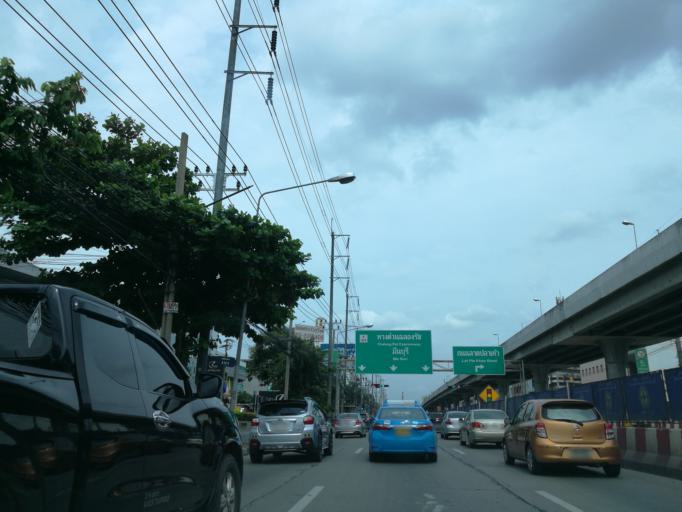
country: TH
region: Bangkok
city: Bang Khen
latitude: 13.8657
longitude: 100.6126
